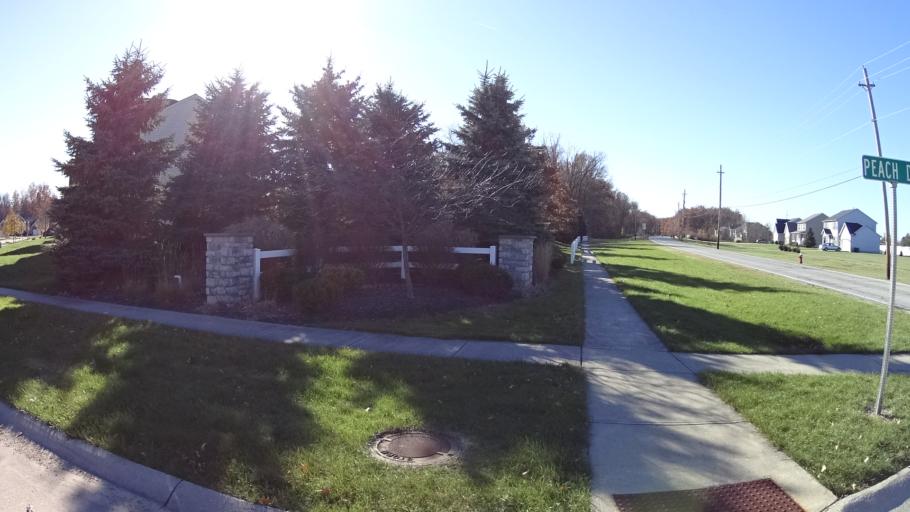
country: US
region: Ohio
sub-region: Lorain County
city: Avon Center
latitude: 41.4676
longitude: -81.9769
